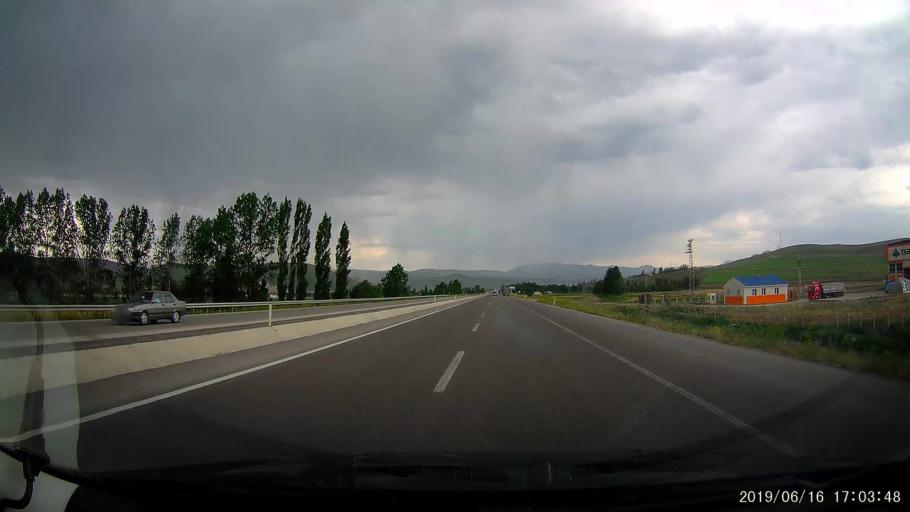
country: TR
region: Erzurum
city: Askale
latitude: 39.9329
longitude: 40.7234
